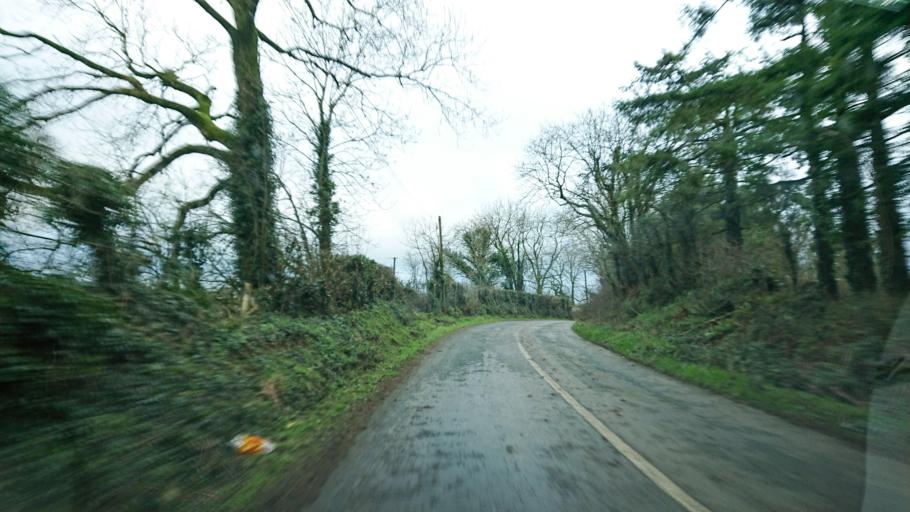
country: IE
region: Munster
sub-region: Waterford
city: Portlaw
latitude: 52.2531
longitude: -7.4083
